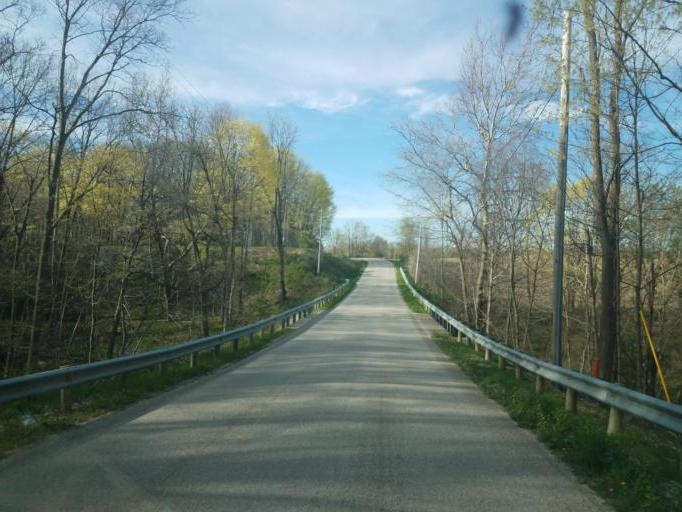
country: US
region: Ohio
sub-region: Morrow County
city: Mount Gilead
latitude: 40.5983
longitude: -82.7761
